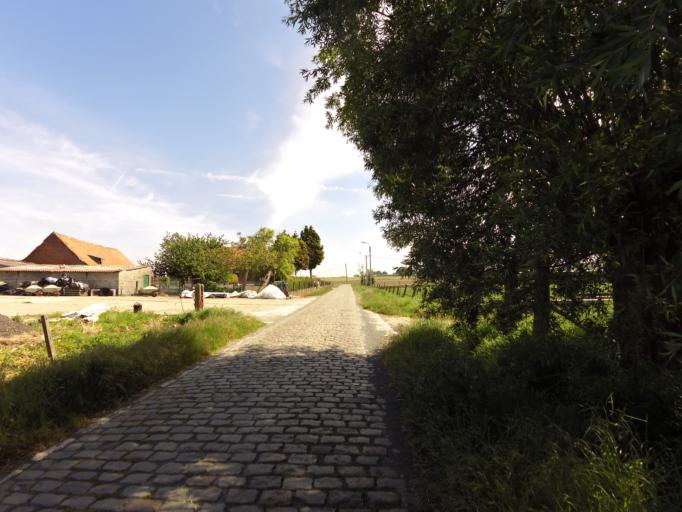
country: BE
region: Flanders
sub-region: Provincie West-Vlaanderen
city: Ichtegem
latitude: 51.0928
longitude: 3.0299
